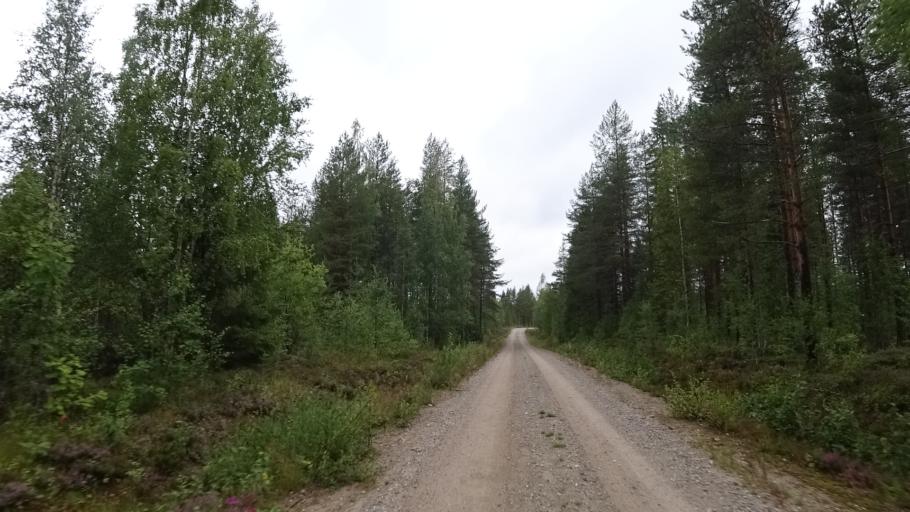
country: FI
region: North Karelia
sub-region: Pielisen Karjala
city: Lieksa
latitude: 63.5068
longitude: 30.1499
